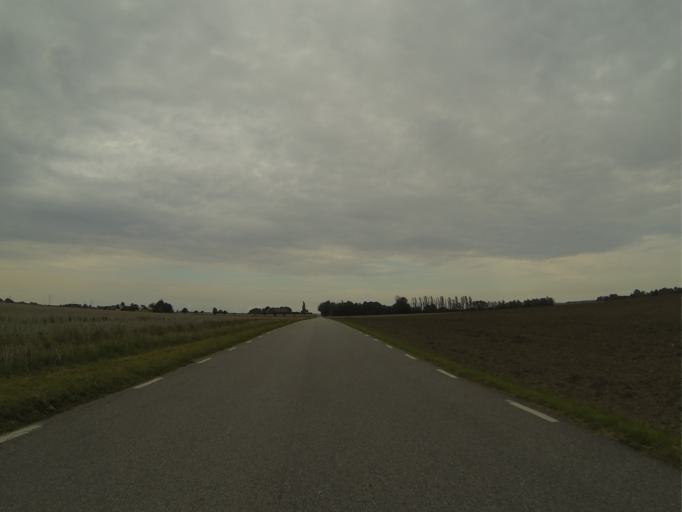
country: SE
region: Skane
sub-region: Staffanstorps Kommun
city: Hjaerup
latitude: 55.6432
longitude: 13.1497
